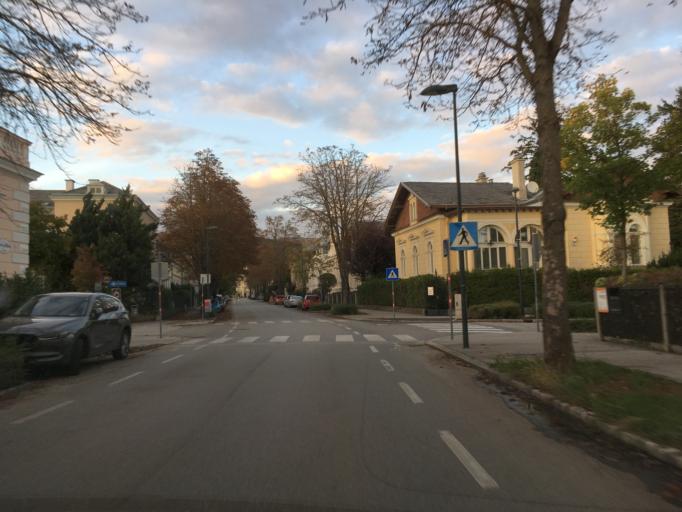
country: AT
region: Lower Austria
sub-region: Politischer Bezirk Baden
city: Baden
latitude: 48.0085
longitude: 16.2442
